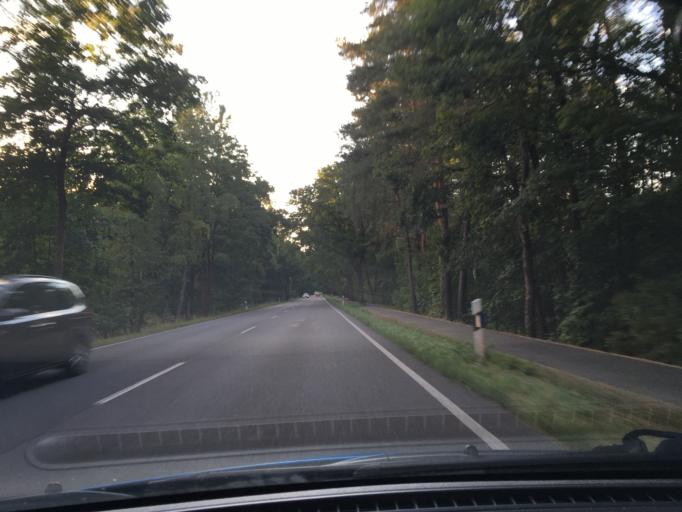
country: DE
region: Lower Saxony
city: Celle
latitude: 52.6632
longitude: 10.0457
